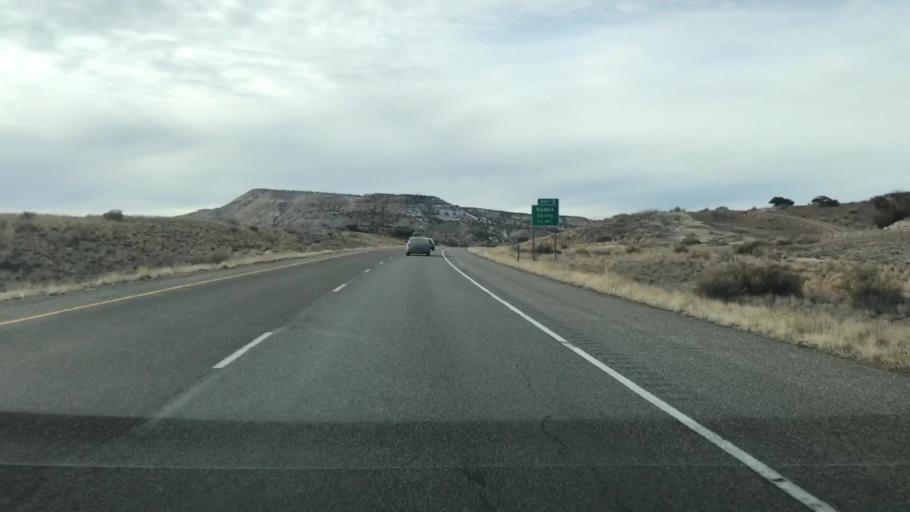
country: US
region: Colorado
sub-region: Mesa County
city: Loma
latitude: 39.1938
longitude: -109.0055
